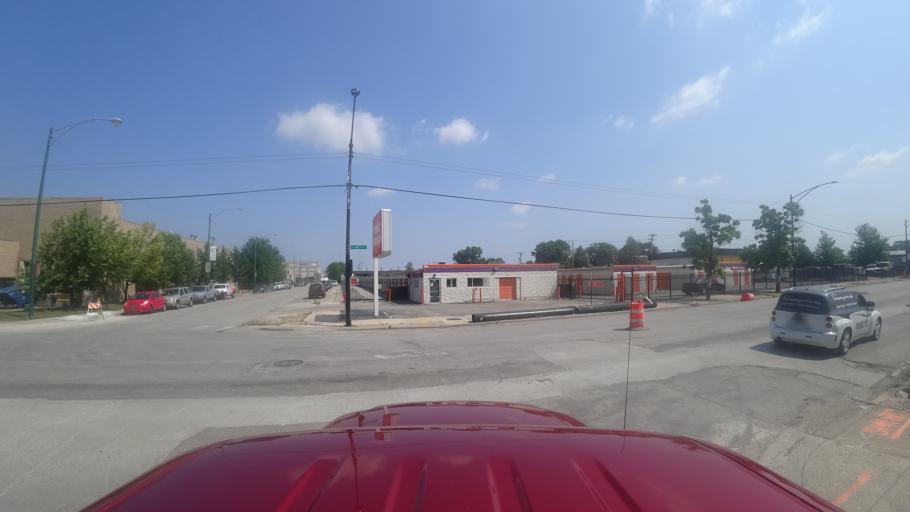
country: US
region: Illinois
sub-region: Cook County
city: Cicero
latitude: 41.8077
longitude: -87.7298
